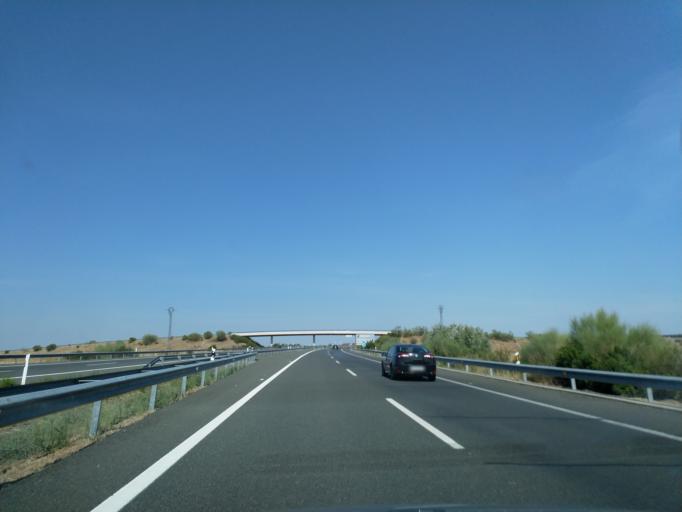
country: ES
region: Extremadura
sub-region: Provincia de Caceres
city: Aldea del Cano
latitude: 39.2825
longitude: -6.3275
